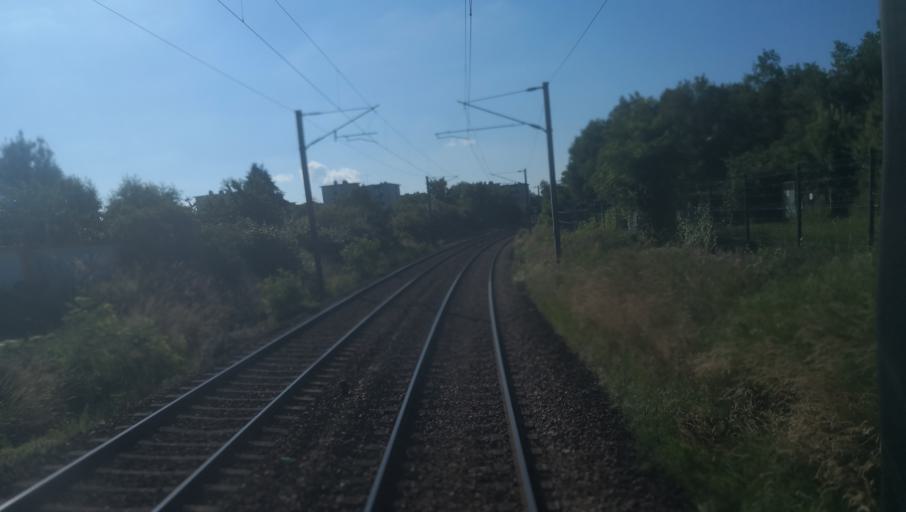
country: FR
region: Centre
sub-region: Departement du Loiret
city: Gien
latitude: 47.6906
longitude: 2.6419
